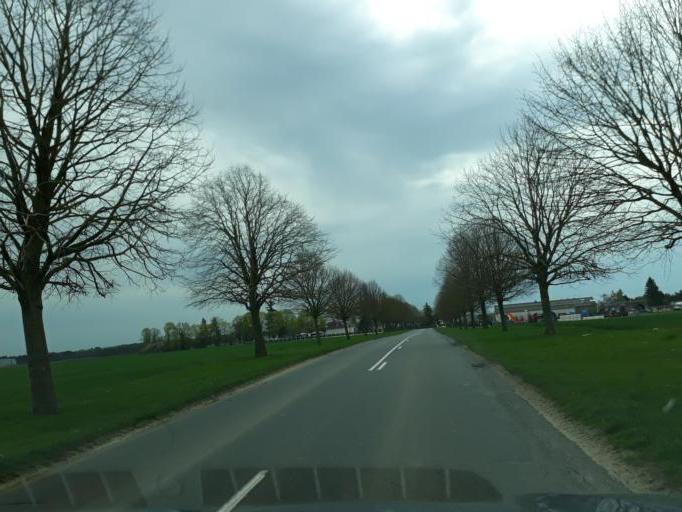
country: FR
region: Centre
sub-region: Departement du Loiret
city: Epieds-en-Beauce
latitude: 47.9425
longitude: 1.6214
